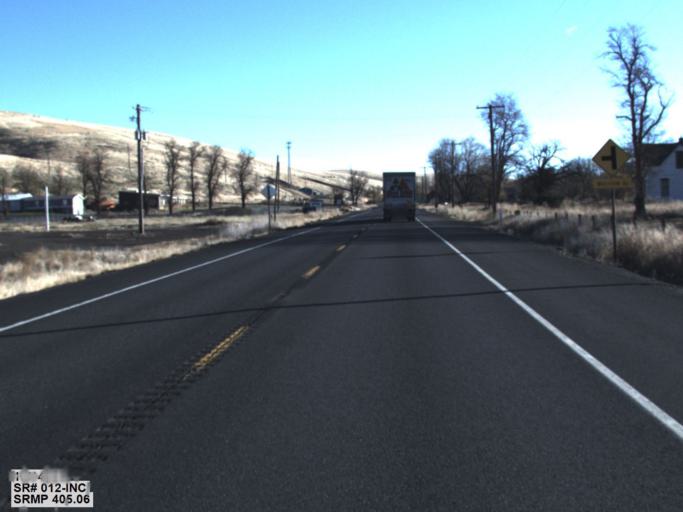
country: US
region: Washington
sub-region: Garfield County
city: Pomeroy
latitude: 46.4748
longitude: -117.5672
